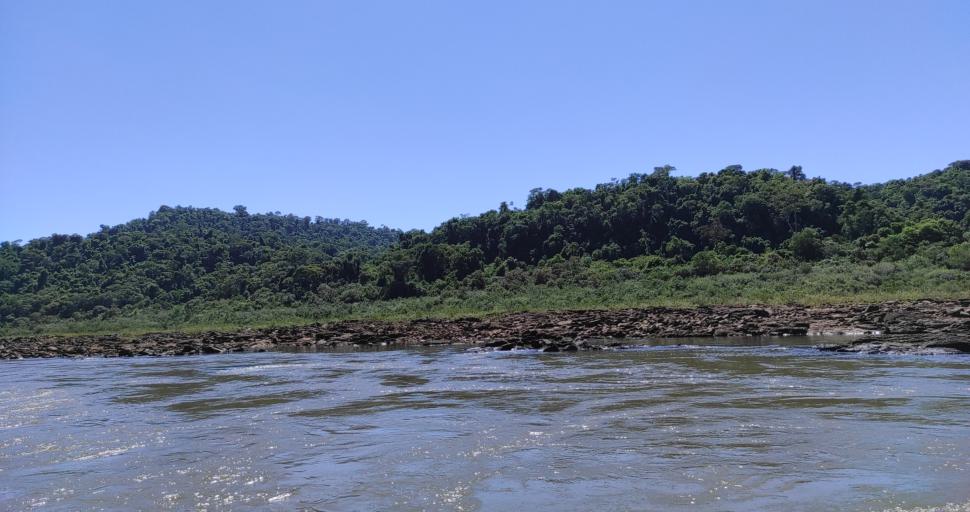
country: BR
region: Rio Grande do Sul
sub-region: Tres Passos
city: Tres Passos
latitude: -27.1551
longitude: -53.8893
